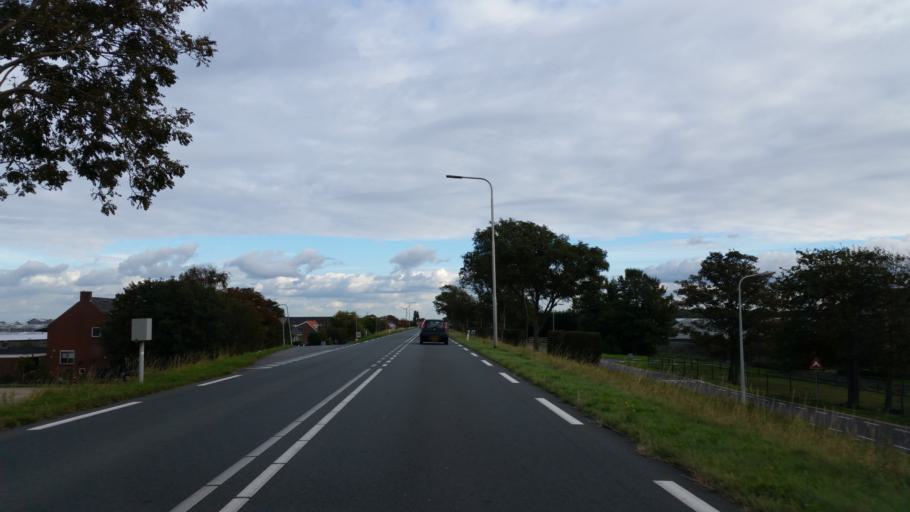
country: NL
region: South Holland
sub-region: Gemeente Westland
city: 's-Gravenzande
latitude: 51.9840
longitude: 4.1705
